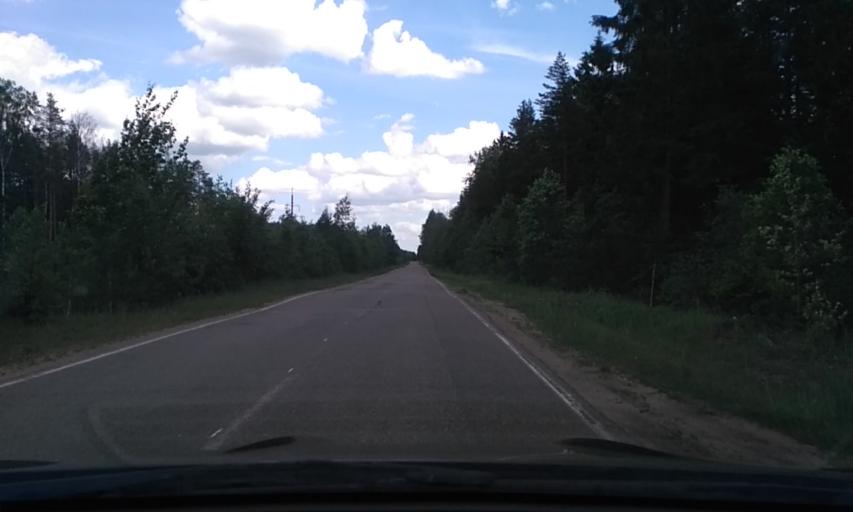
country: RU
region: Leningrad
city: Otradnoye
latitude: 59.8197
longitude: 30.8121
